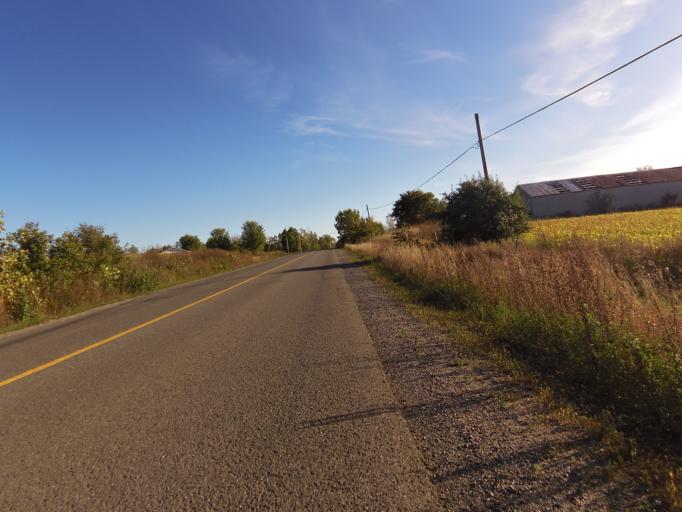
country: CA
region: Ontario
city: Bells Corners
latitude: 45.4396
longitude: -75.8807
